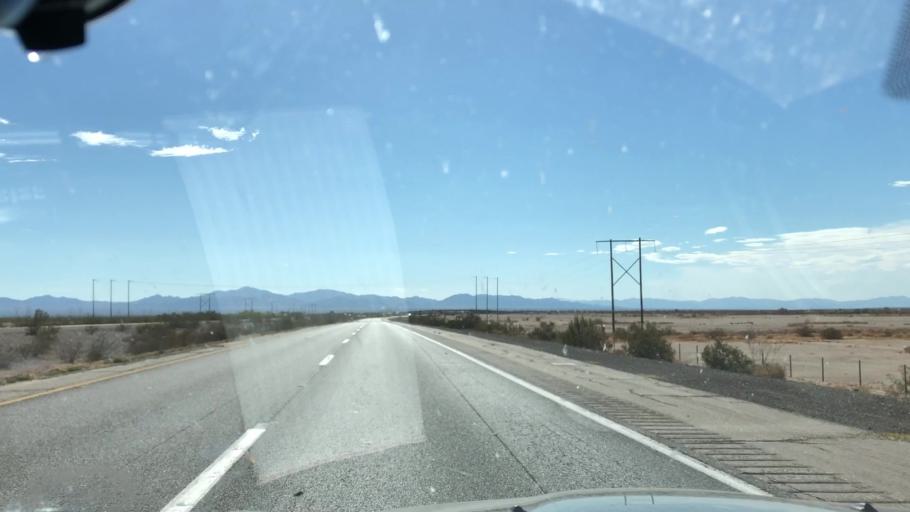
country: US
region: California
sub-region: Riverside County
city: Mesa Verde
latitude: 33.6062
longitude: -114.9748
